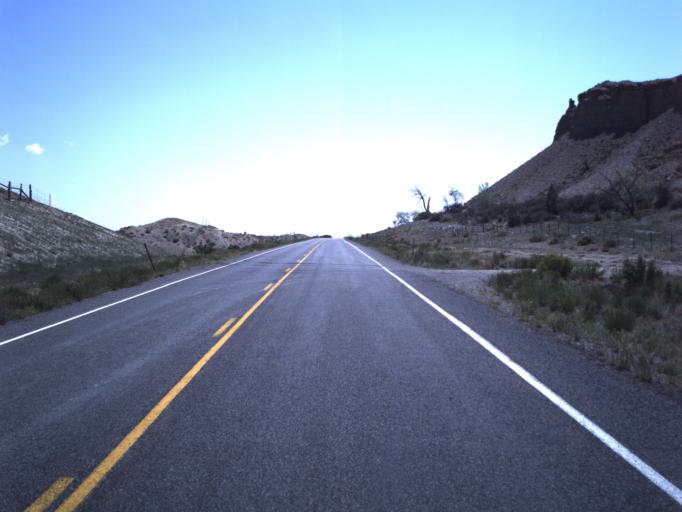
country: US
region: Utah
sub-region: Emery County
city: Orangeville
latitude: 39.2335
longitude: -111.0811
